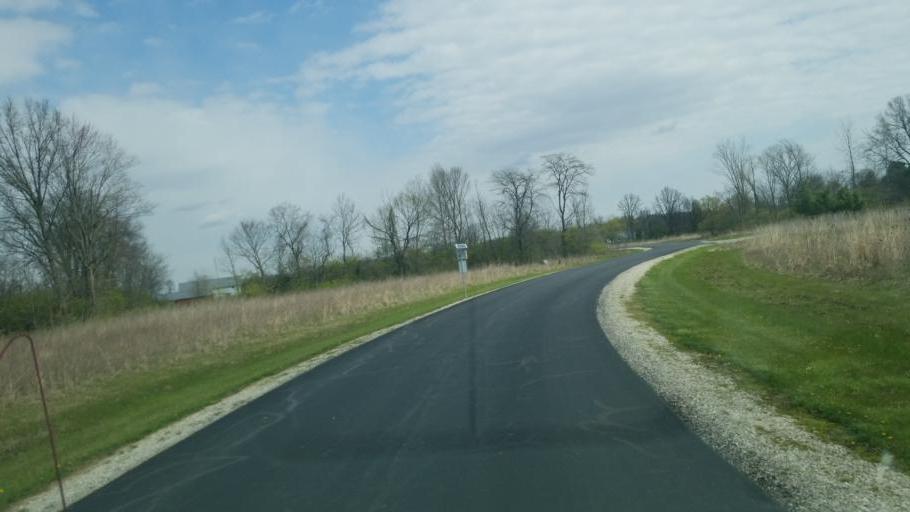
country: US
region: Ohio
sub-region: Delaware County
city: Delaware
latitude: 40.3478
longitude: -83.1152
